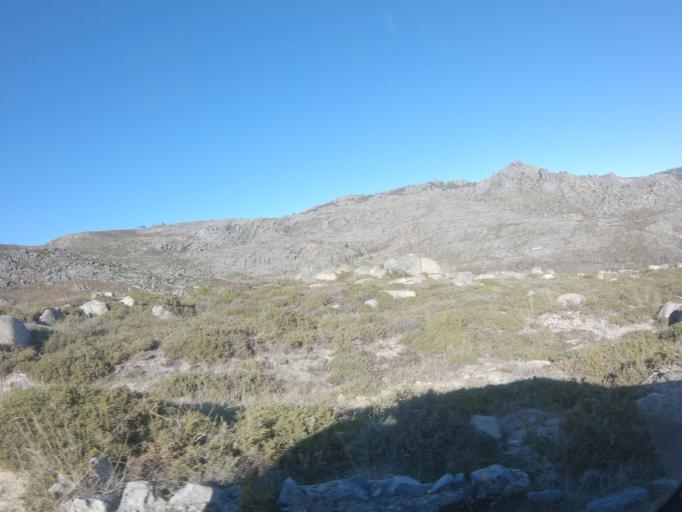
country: PT
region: Vila Real
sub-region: Vila Real
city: Vila Real
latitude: 41.3318
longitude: -7.8094
